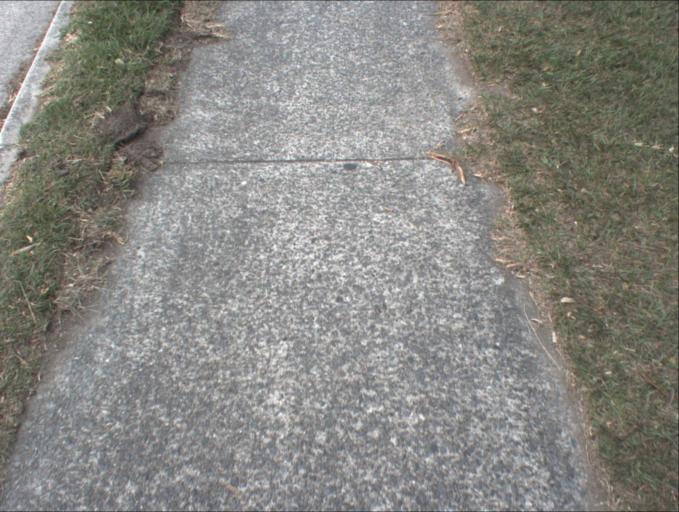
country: AU
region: Queensland
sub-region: Logan
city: Woodridge
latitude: -27.6631
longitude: 153.0569
